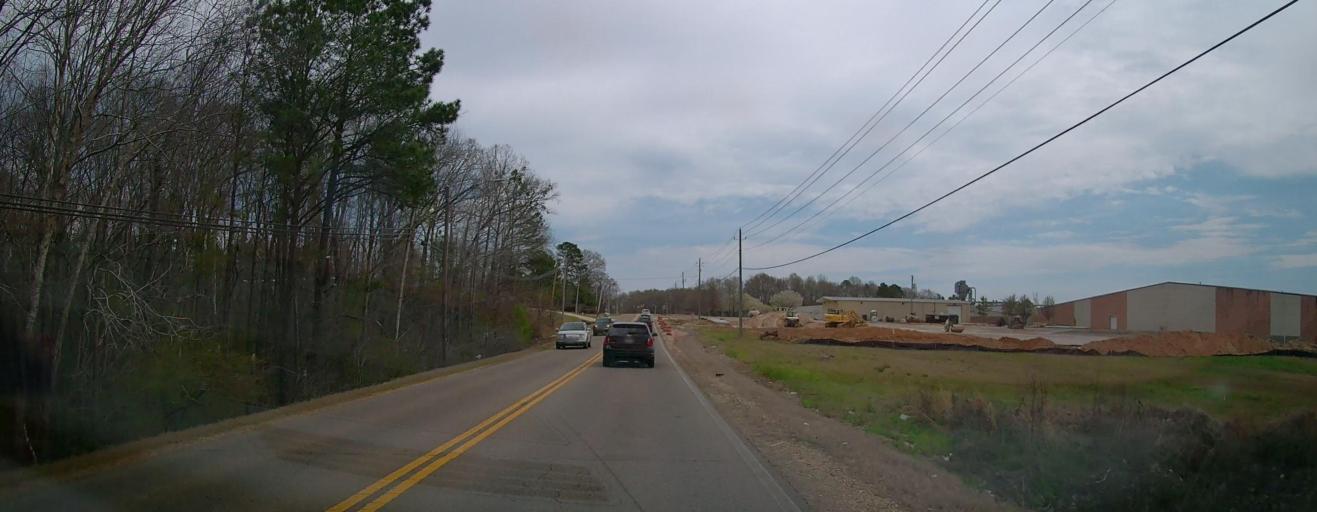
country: US
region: Mississippi
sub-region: Lee County
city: Tupelo
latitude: 34.2580
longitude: -88.6607
